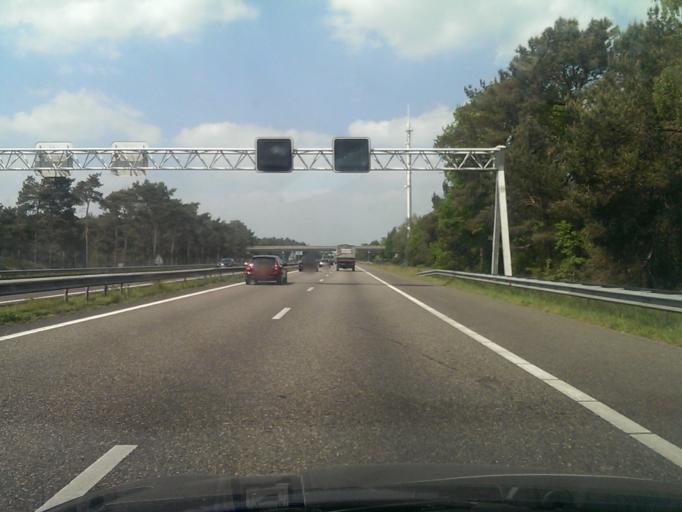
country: NL
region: North Brabant
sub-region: Gemeente Heeze-Leende
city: Heeze
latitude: 51.3638
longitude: 5.5298
